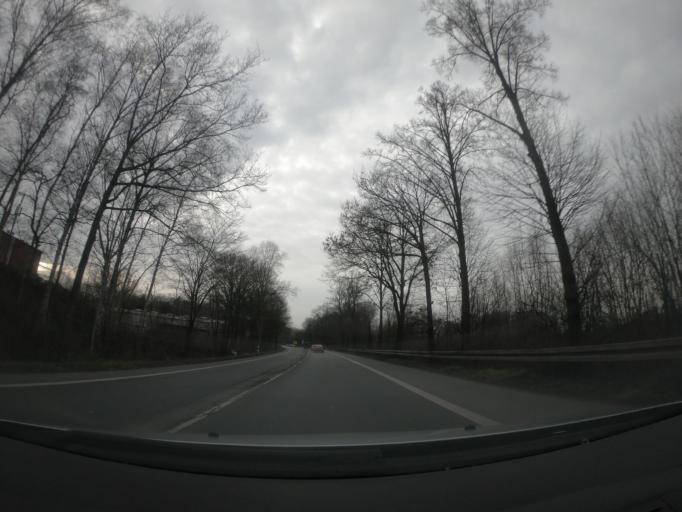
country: DE
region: North Rhine-Westphalia
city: Lunen
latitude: 51.6032
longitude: 7.4845
